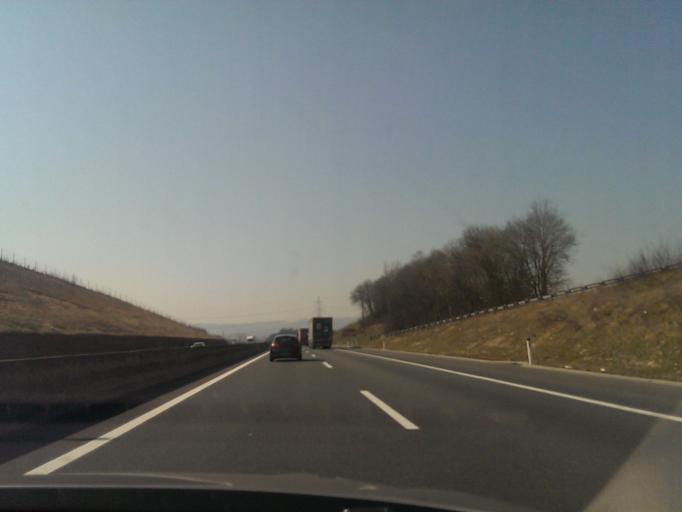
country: AT
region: Upper Austria
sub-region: Politischer Bezirk Vocklabruck
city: Niederthalheim
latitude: 48.1780
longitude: 13.7442
